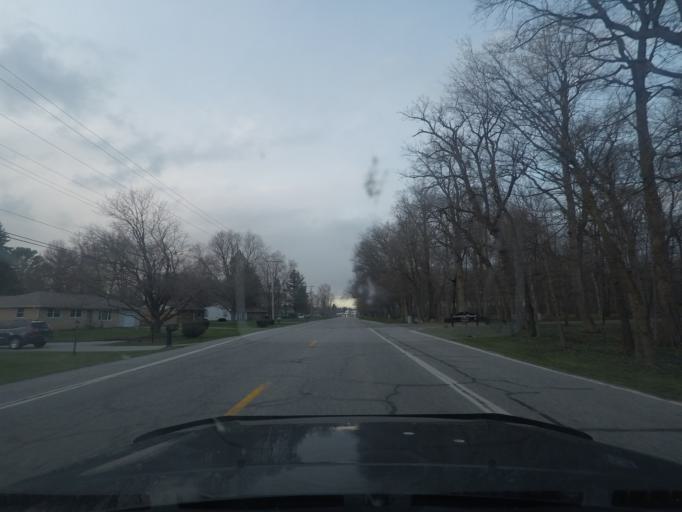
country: US
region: Indiana
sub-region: LaPorte County
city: LaPorte
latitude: 41.5955
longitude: -86.7392
